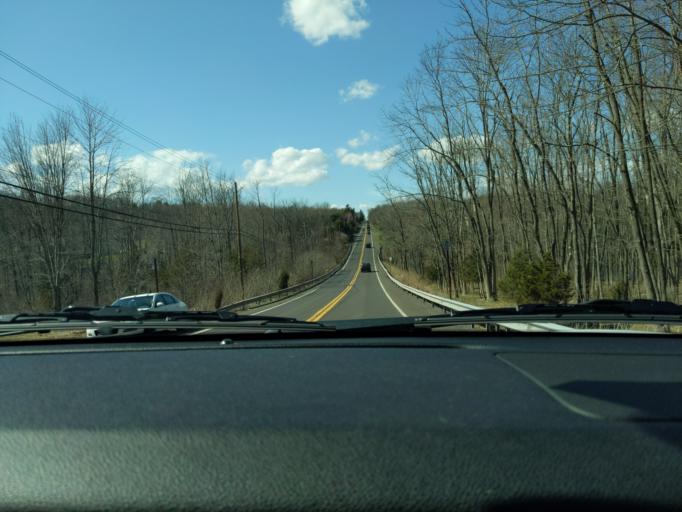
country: US
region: Pennsylvania
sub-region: Bucks County
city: Perkasie
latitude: 40.4150
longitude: -75.2695
